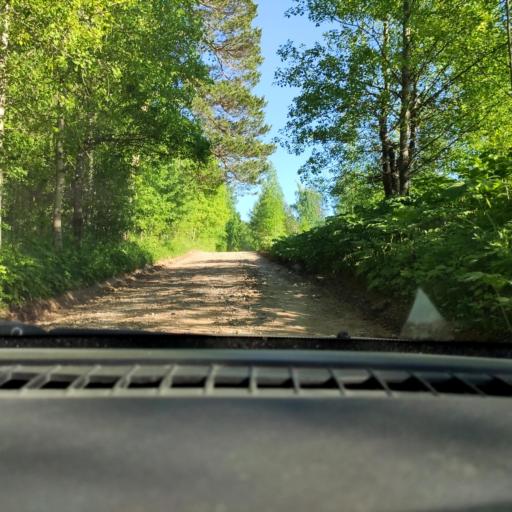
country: RU
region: Perm
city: Overyata
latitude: 58.1256
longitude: 55.8771
